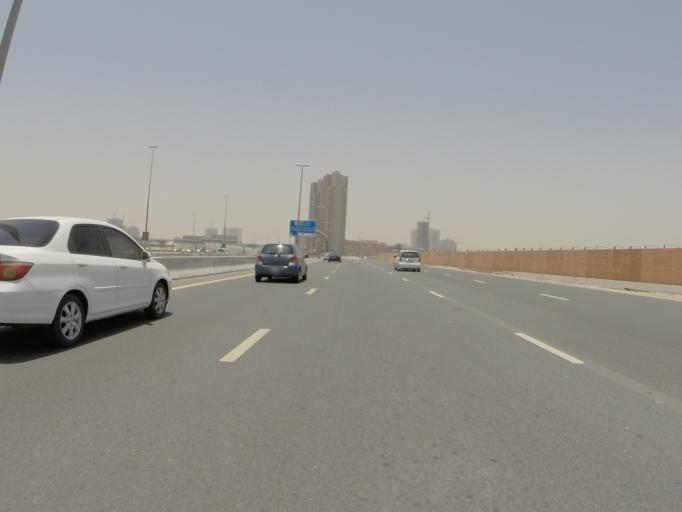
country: AE
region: Dubai
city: Dubai
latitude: 25.0540
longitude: 55.1947
